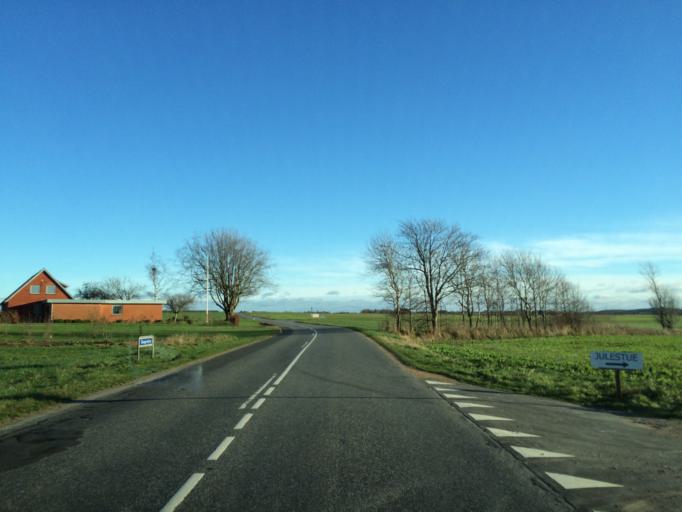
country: DK
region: Central Jutland
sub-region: Ringkobing-Skjern Kommune
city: Videbaek
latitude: 56.0845
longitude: 8.6516
